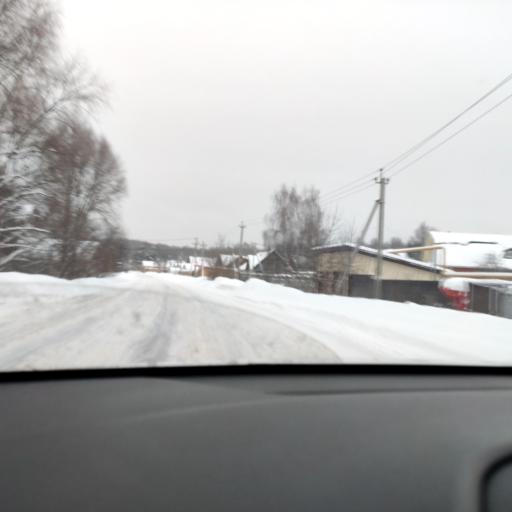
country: RU
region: Tatarstan
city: Vysokaya Gora
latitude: 55.9577
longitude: 49.1580
